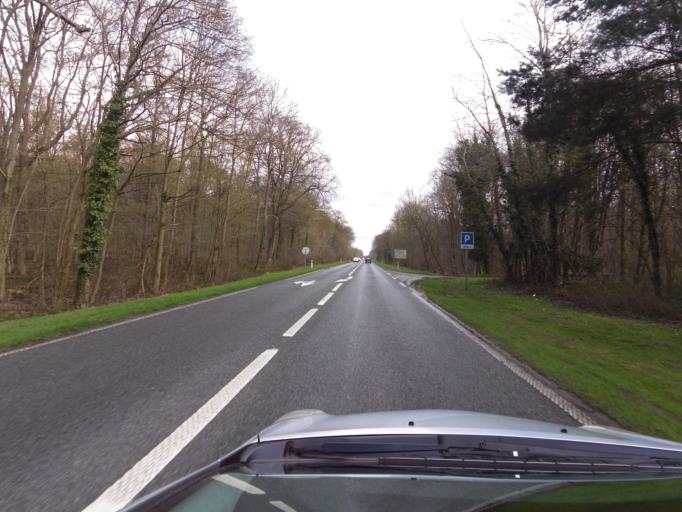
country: FR
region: Picardie
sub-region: Departement de l'Oise
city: Fleurines
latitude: 49.2750
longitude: 2.5928
